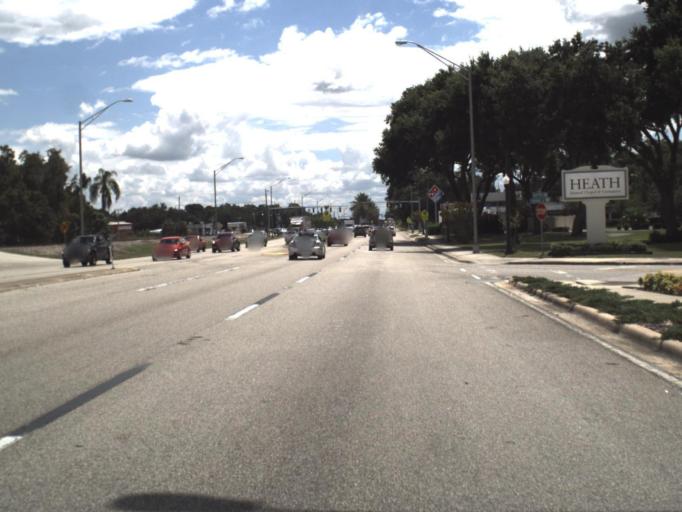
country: US
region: Florida
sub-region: Polk County
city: Lakeland
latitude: 28.0420
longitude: -81.9448
